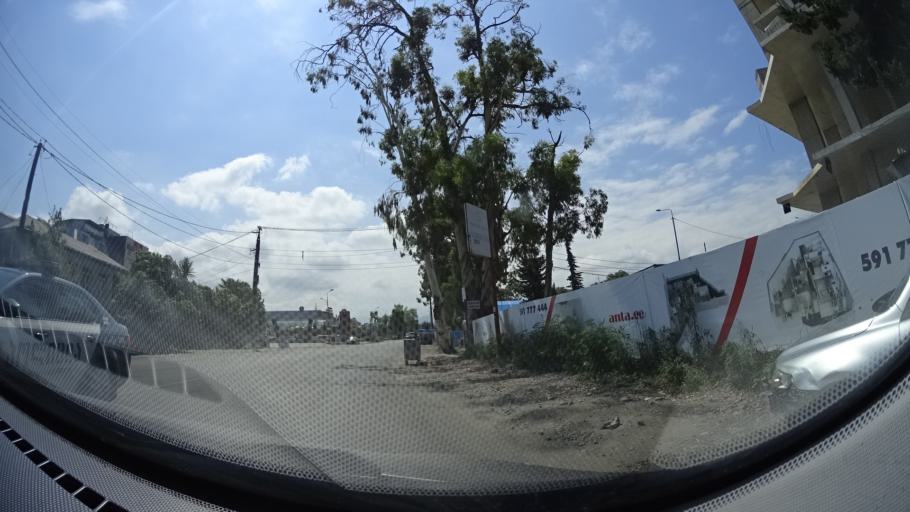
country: GE
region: Ajaria
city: Batumi
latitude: 41.6222
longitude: 41.6154
